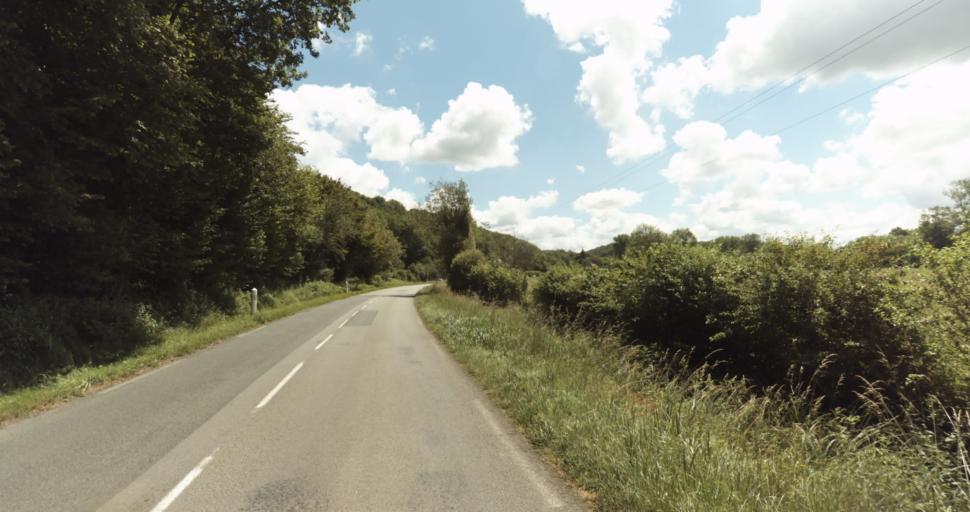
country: FR
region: Aquitaine
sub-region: Departement de la Dordogne
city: Beaumont-du-Perigord
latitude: 44.7987
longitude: 0.7466
